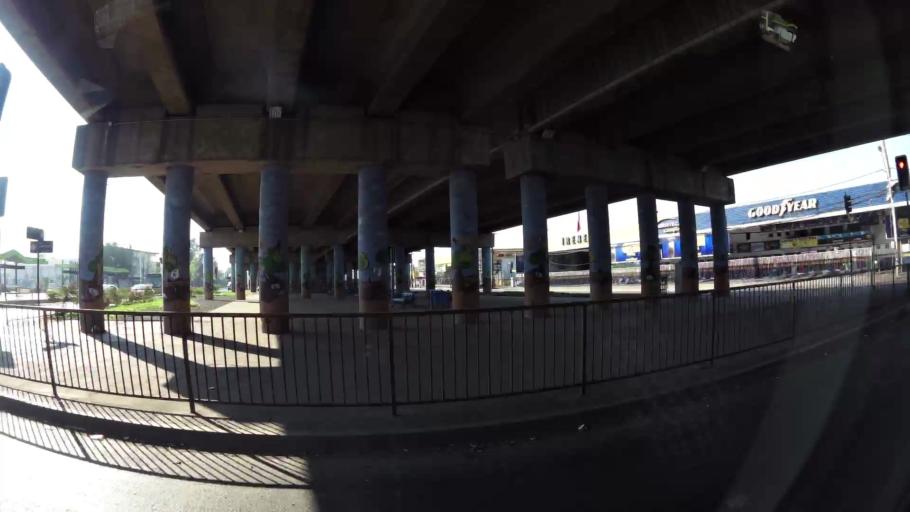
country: CL
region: Santiago Metropolitan
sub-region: Provincia de Santiago
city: Lo Prado
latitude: -33.4030
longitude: -70.6820
